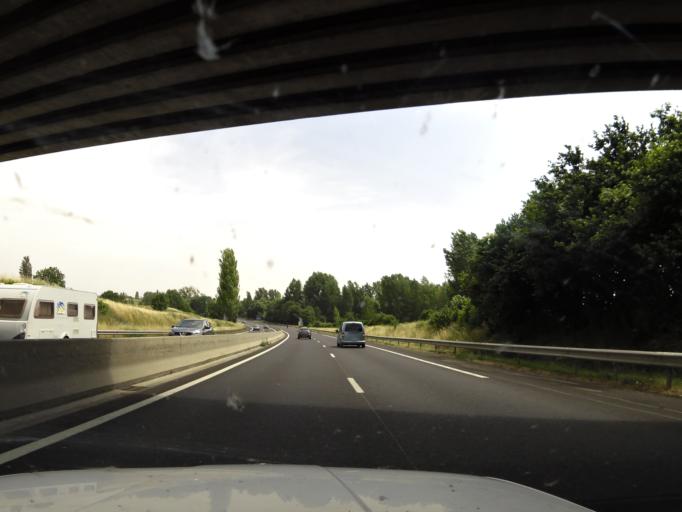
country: FR
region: Auvergne
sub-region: Departement du Puy-de-Dome
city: Tallende
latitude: 45.6684
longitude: 3.1433
